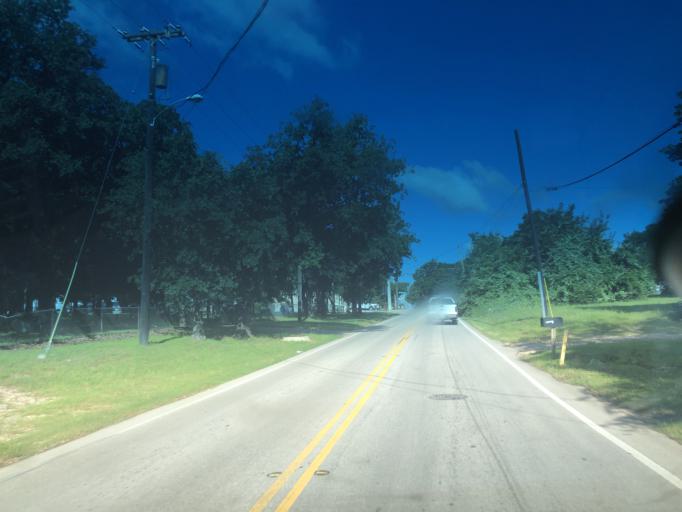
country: US
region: Texas
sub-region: Dallas County
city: Grand Prairie
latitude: 32.8035
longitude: -97.0193
